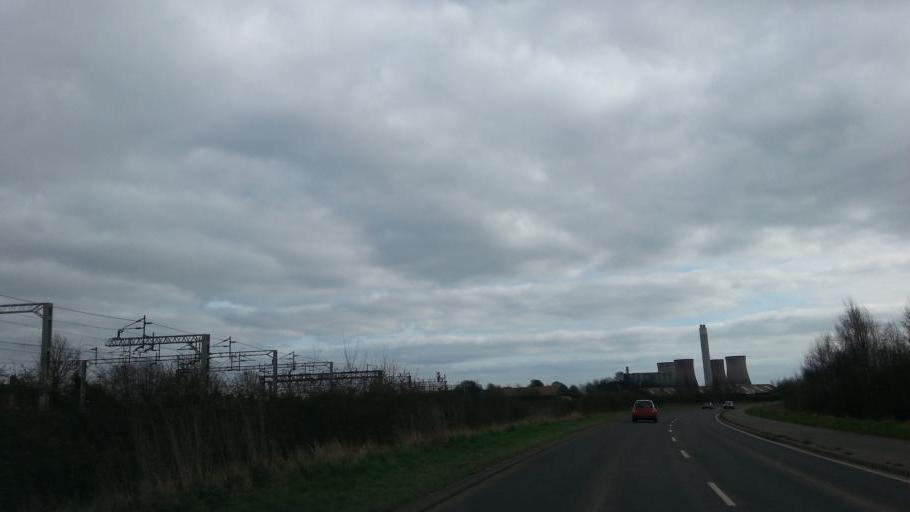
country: GB
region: England
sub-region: Staffordshire
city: Rugeley
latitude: 52.7725
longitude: -1.9348
